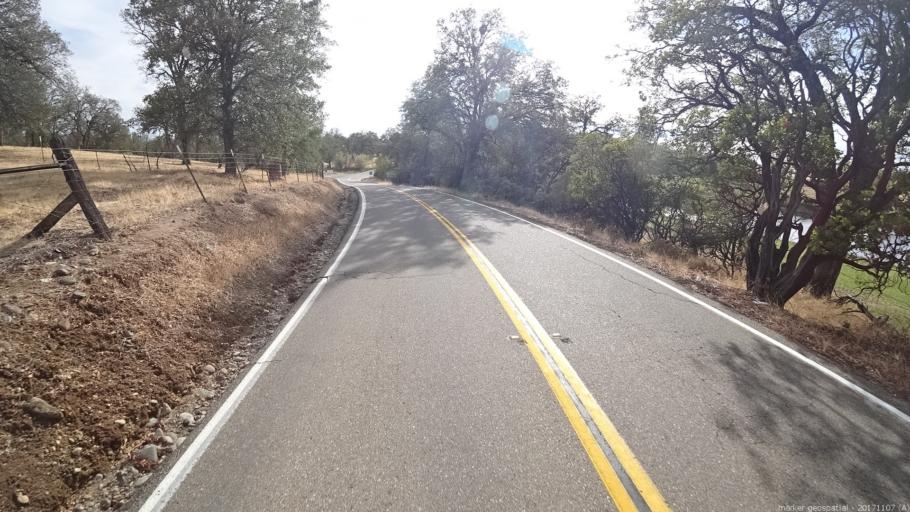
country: US
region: California
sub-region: Shasta County
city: Shasta
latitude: 40.5076
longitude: -122.5387
